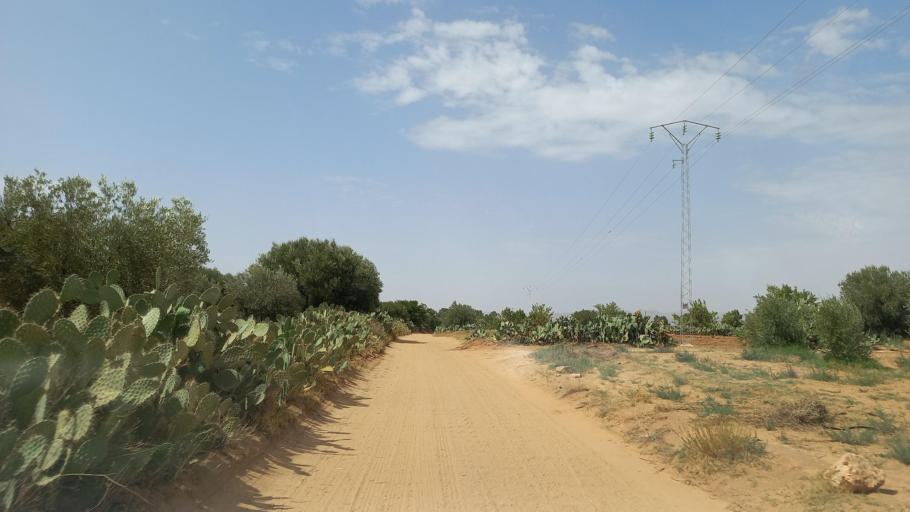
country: TN
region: Al Qasrayn
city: Kasserine
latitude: 35.2591
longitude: 9.0530
